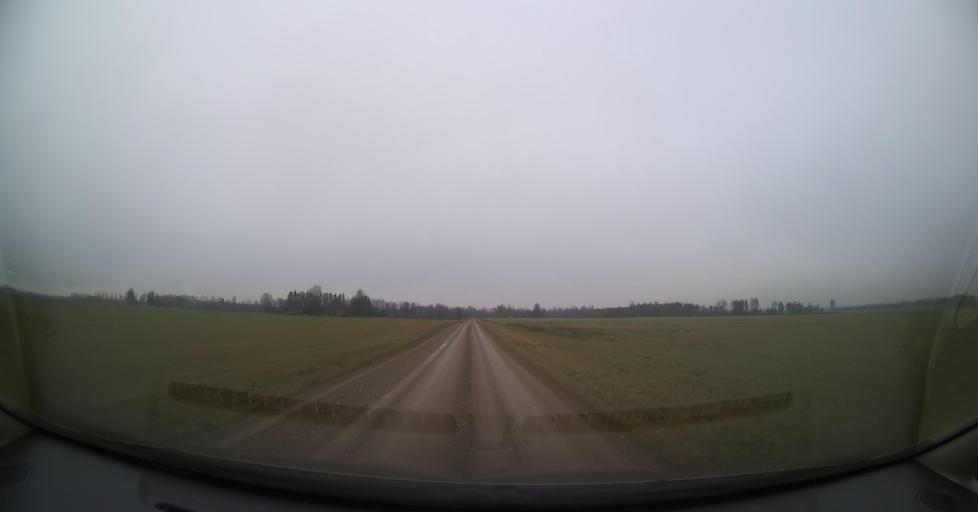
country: EE
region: Tartu
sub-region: Tartu linn
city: Tartu
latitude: 58.3865
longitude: 26.9275
